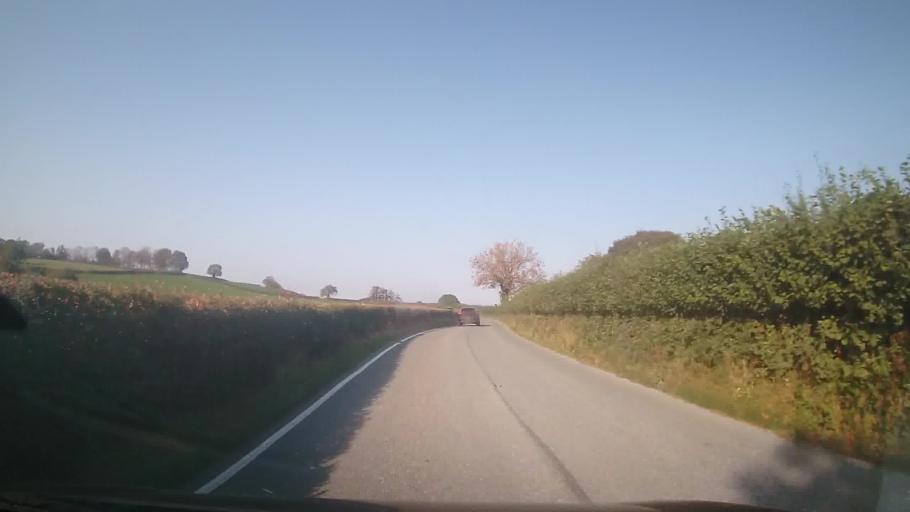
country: GB
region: Wales
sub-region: County of Ceredigion
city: Llangybi
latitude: 52.1968
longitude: -3.9710
